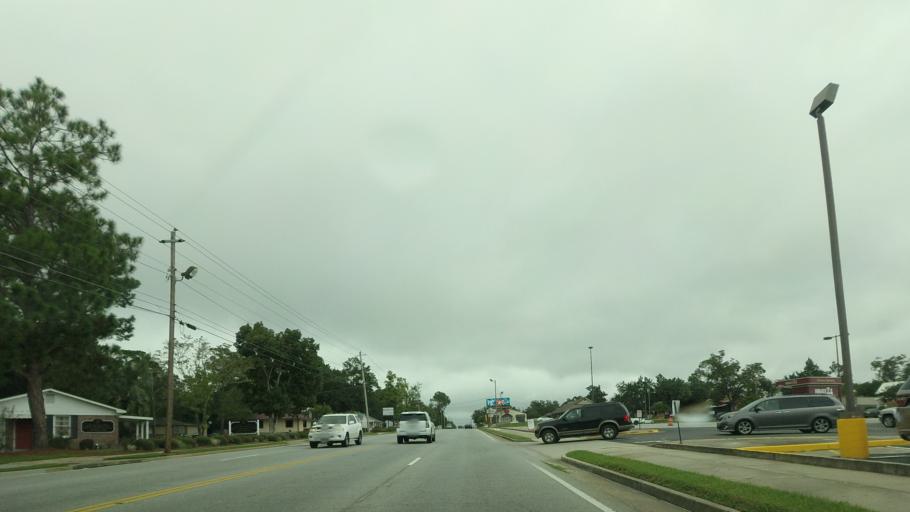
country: US
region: Georgia
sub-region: Lowndes County
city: Remerton
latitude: 30.8469
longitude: -83.3103
